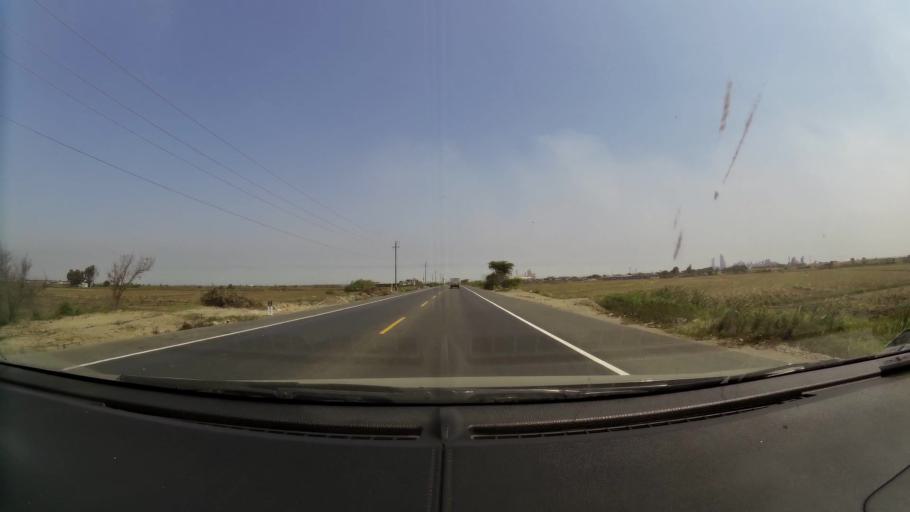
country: PE
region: La Libertad
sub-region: Provincia de Pacasmayo
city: San Pedro de Lloc
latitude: -7.4191
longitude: -79.5361
